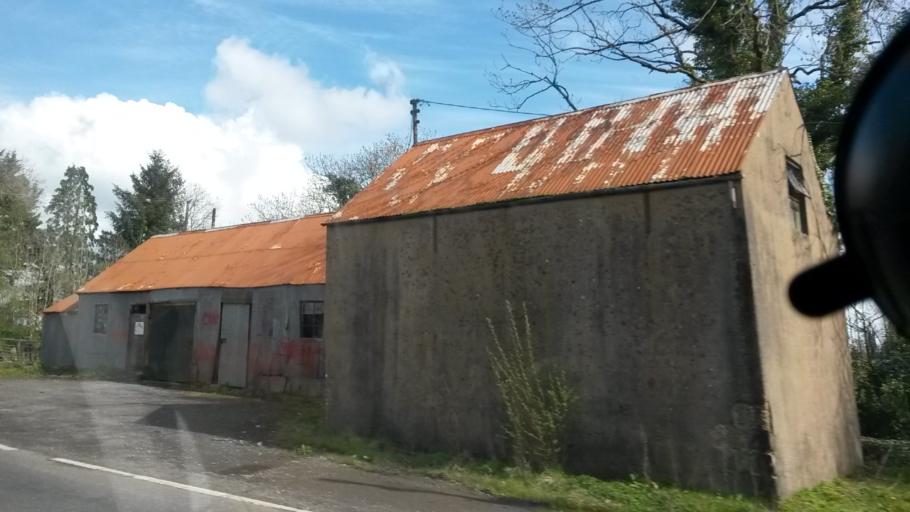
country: IE
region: Ulster
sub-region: An Cabhan
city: Ballyconnell
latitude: 54.1487
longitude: -7.5202
